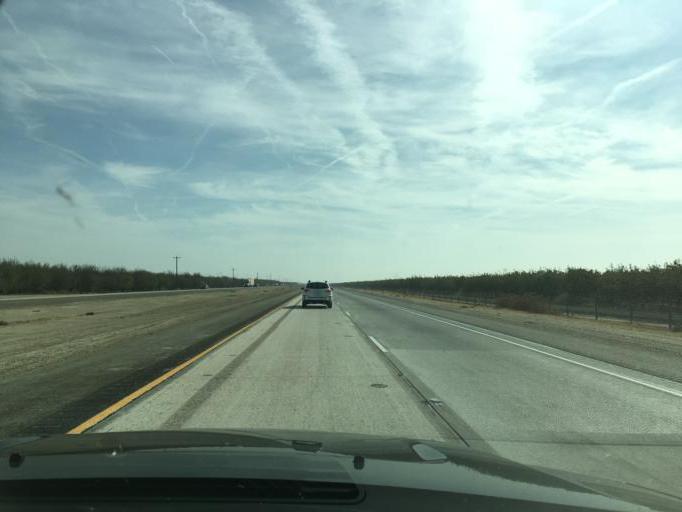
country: US
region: California
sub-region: Kern County
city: Lost Hills
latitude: 35.5276
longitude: -119.5650
